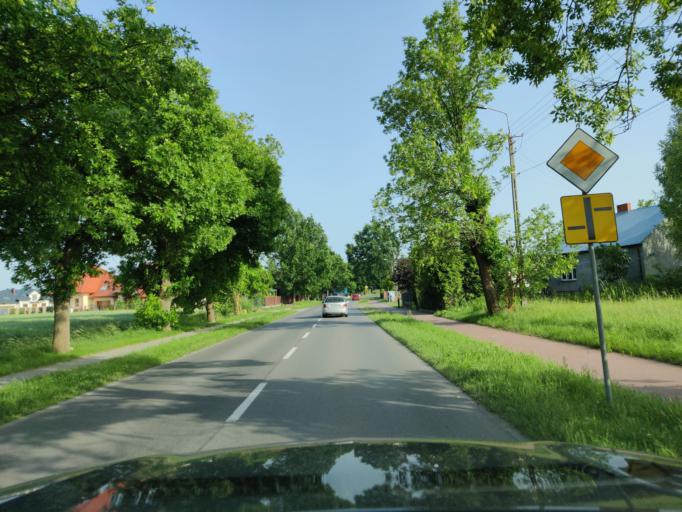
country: PL
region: Masovian Voivodeship
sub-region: Powiat wyszkowski
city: Wyszkow
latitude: 52.6496
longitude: 21.4489
